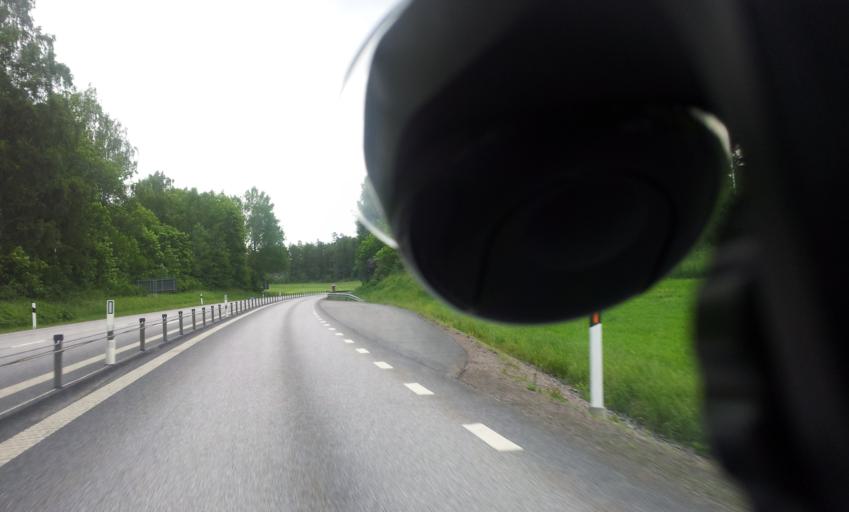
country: SE
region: Kalmar
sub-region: Vasterviks Kommun
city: Forserum
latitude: 57.9585
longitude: 16.4435
